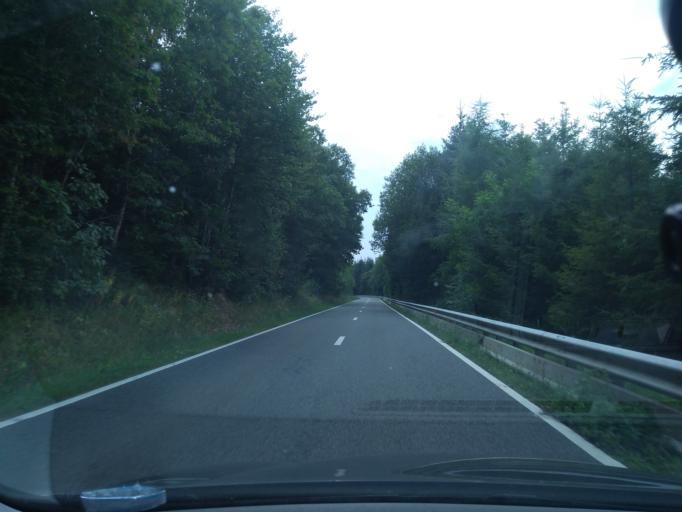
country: BE
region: Wallonia
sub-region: Province du Luxembourg
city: Houffalize
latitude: 50.1079
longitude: 5.7722
